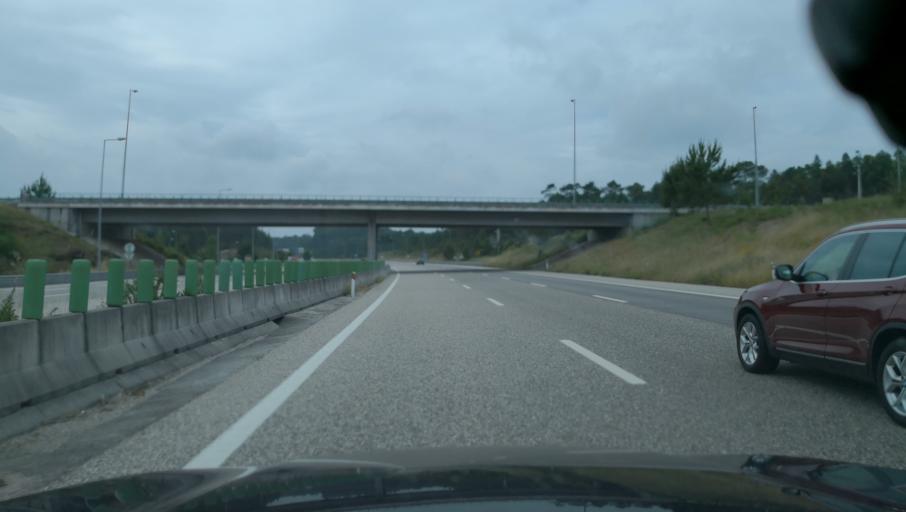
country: PT
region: Coimbra
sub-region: Figueira da Foz
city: Lavos
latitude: 40.0447
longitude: -8.8122
